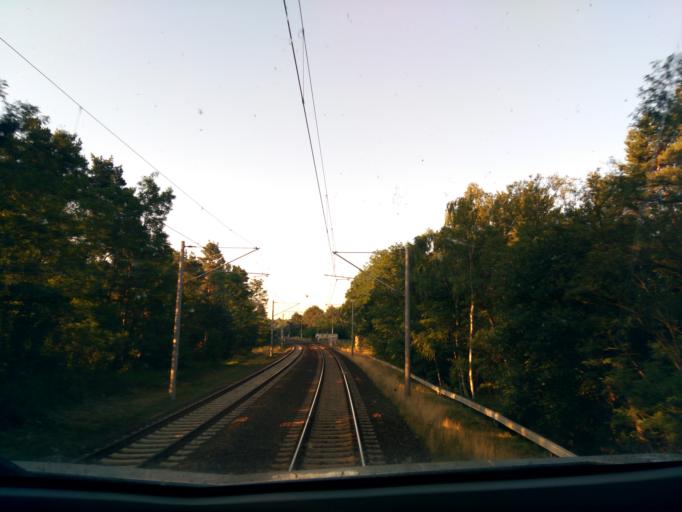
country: DE
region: Brandenburg
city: Schwerin
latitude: 52.1966
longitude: 13.6239
